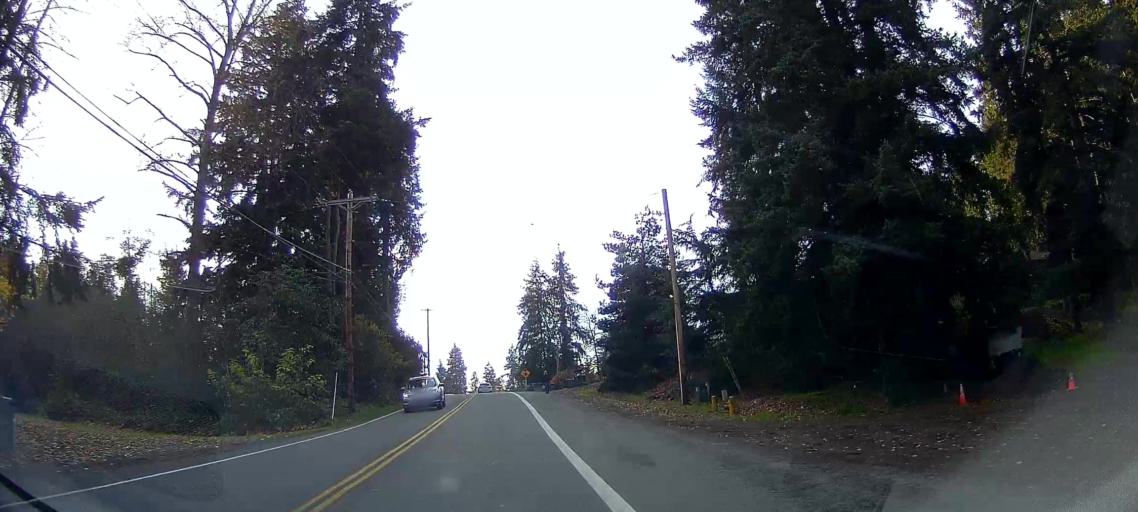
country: US
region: Washington
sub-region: Snohomish County
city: Alderwood Manor
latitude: 47.8083
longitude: -122.2568
